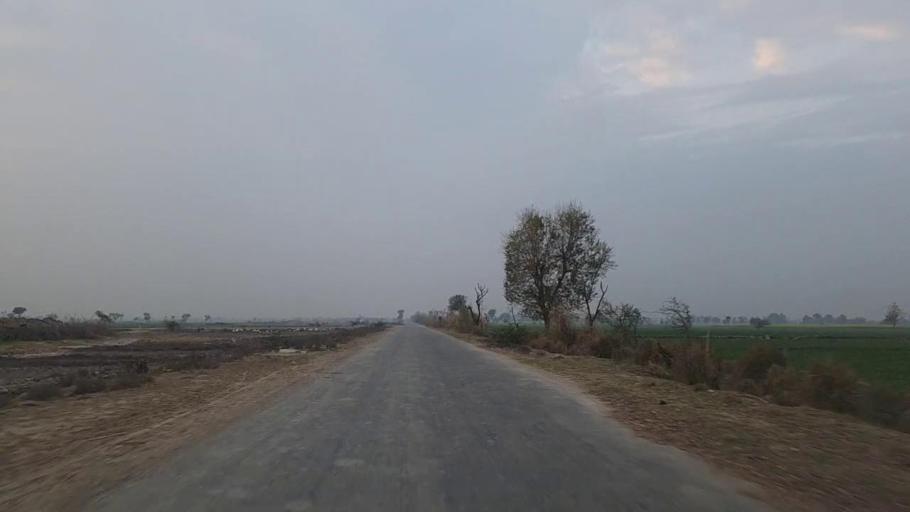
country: PK
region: Sindh
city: Jam Sahib
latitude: 26.3187
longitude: 68.5626
